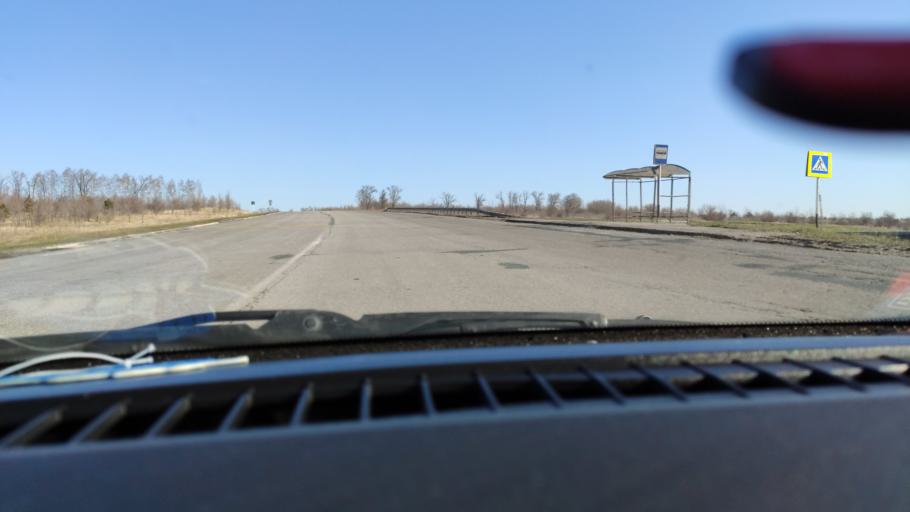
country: RU
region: Samara
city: Varlamovo
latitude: 53.1050
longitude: 48.3569
